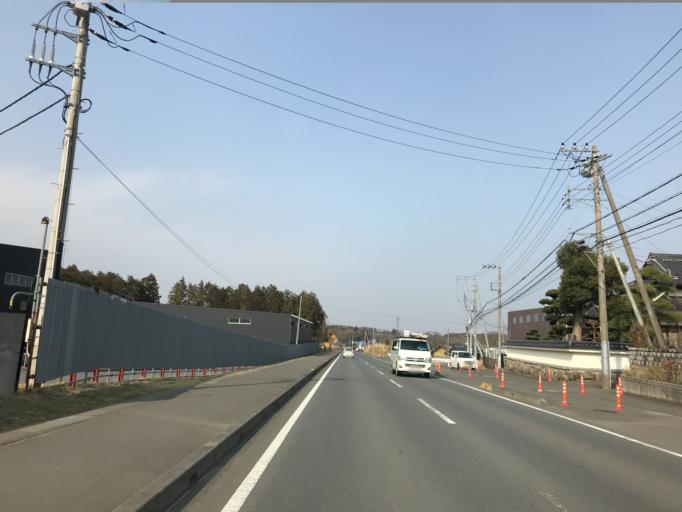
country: JP
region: Ibaraki
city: Okunoya
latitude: 36.2137
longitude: 140.4063
